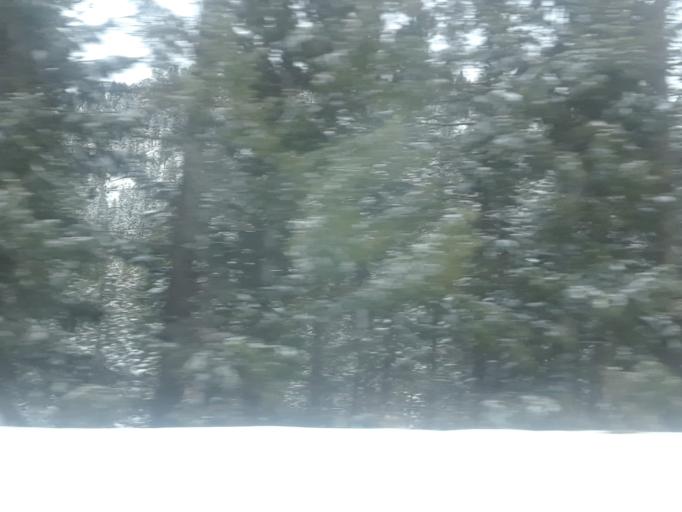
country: US
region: Colorado
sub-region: Boulder County
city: Coal Creek
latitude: 39.9255
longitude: -105.4097
